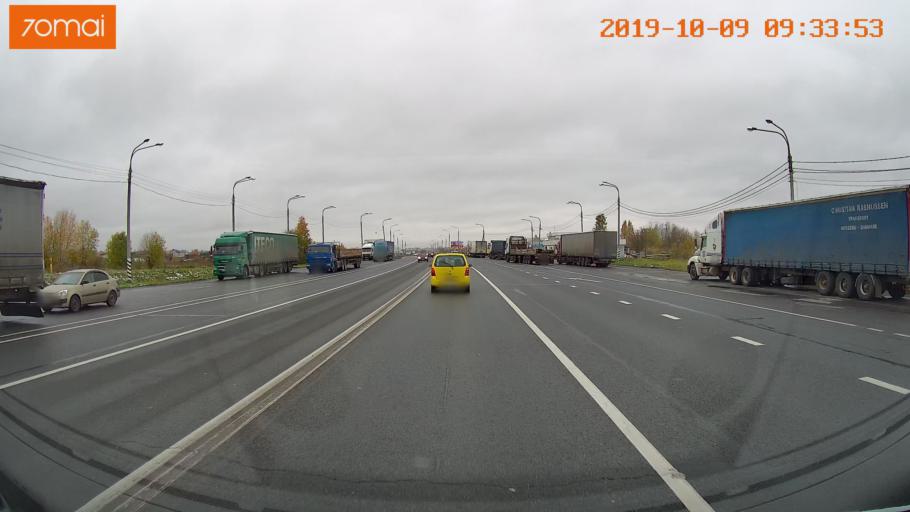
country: RU
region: Vologda
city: Vologda
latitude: 59.1713
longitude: 39.9080
